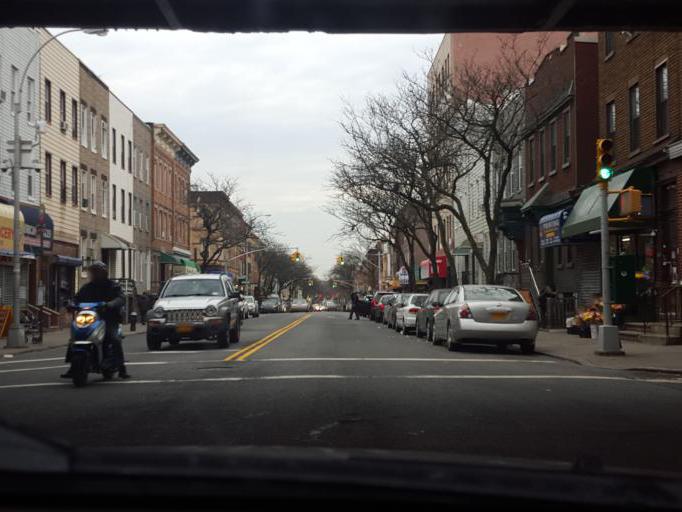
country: US
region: New York
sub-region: Kings County
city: East New York
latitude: 40.7029
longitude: -73.9078
